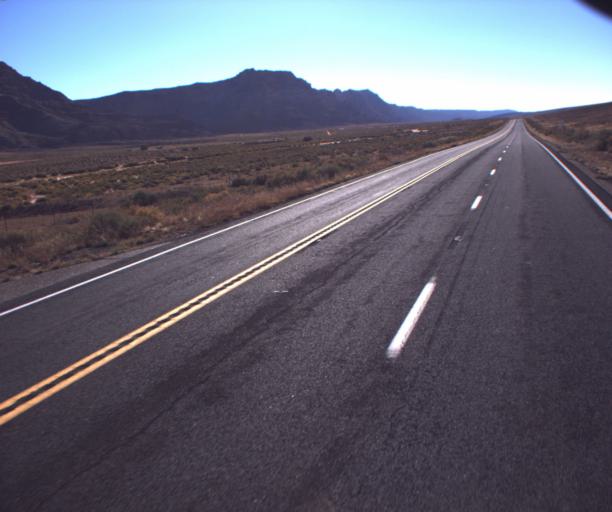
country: US
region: Arizona
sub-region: Coconino County
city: LeChee
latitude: 36.5860
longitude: -111.6506
